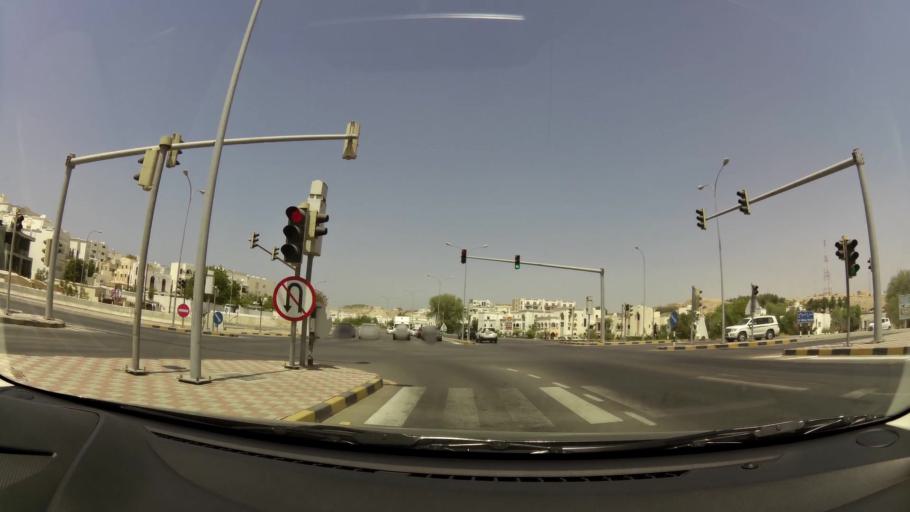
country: OM
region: Muhafazat Masqat
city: Muscat
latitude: 23.6181
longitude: 58.4982
